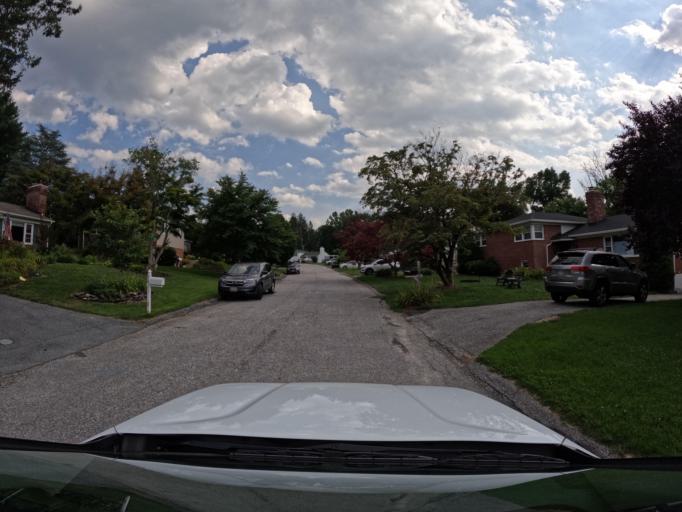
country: US
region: Maryland
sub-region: Baltimore County
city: Lutherville
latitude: 39.4047
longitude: -76.6473
